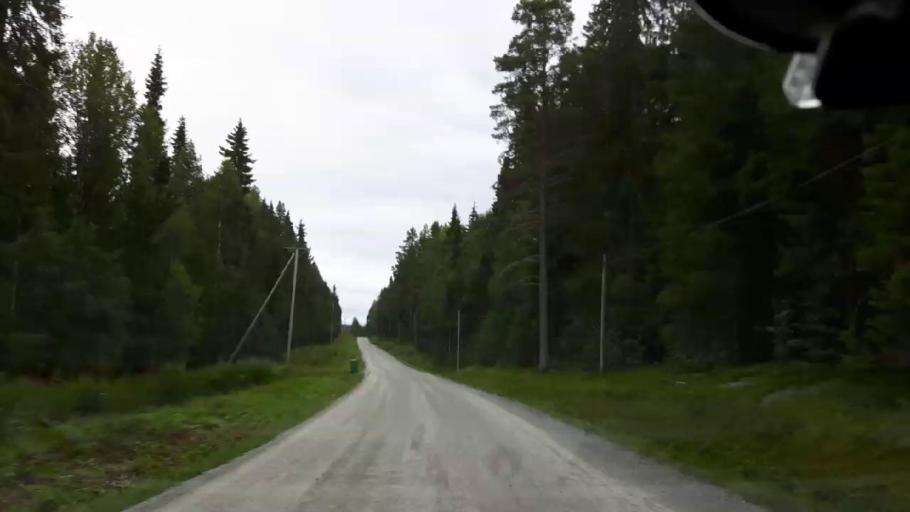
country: SE
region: Jaemtland
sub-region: Braecke Kommun
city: Braecke
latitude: 63.0778
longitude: 15.2894
